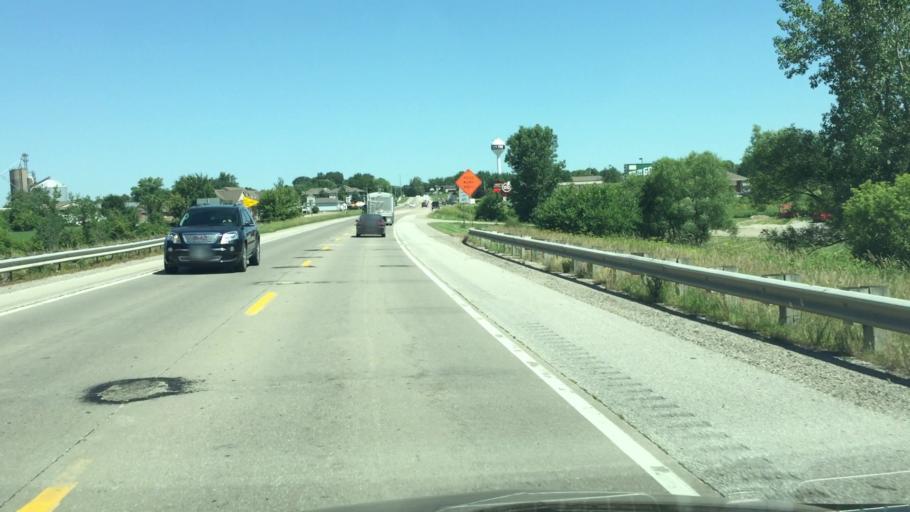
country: US
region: Iowa
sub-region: Johnson County
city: Solon
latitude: 41.7949
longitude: -91.4901
